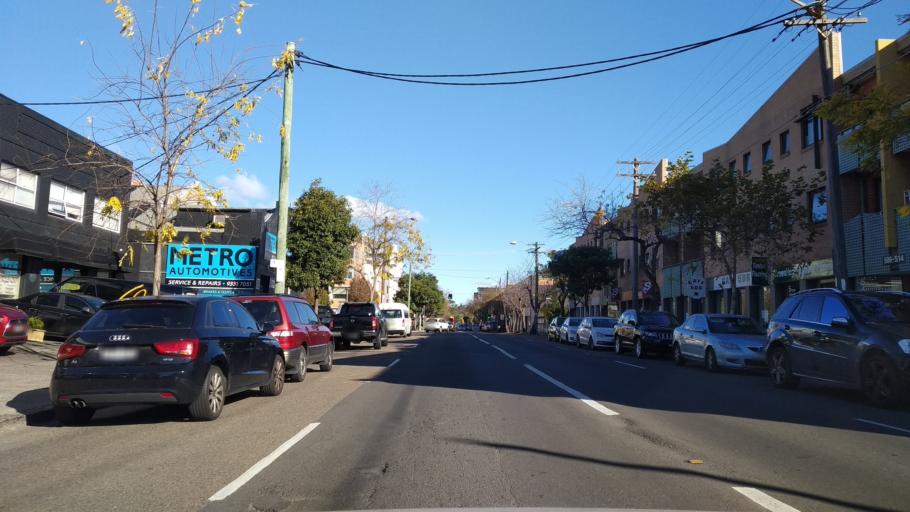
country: AU
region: New South Wales
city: Alexandria
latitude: -33.9133
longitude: 151.2013
